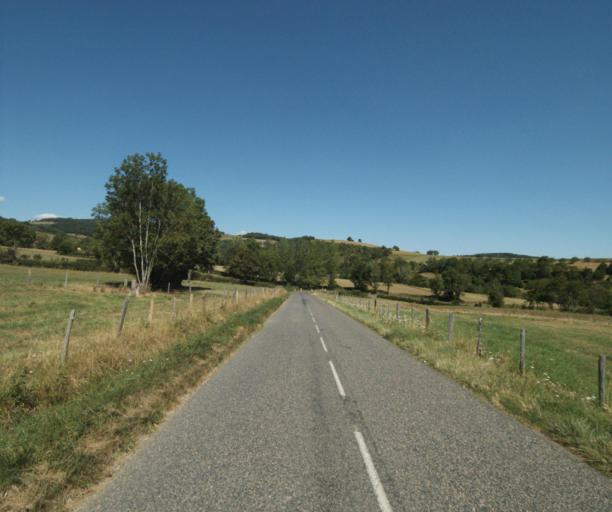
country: FR
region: Rhone-Alpes
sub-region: Departement du Rhone
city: Bessenay
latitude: 45.8001
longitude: 4.5556
